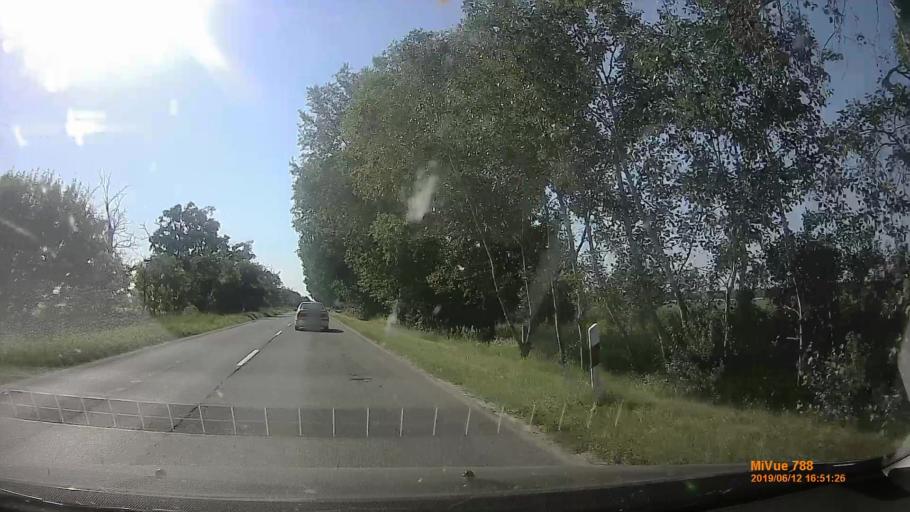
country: HU
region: Csongrad
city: Kiszombor
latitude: 46.2073
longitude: 20.3773
